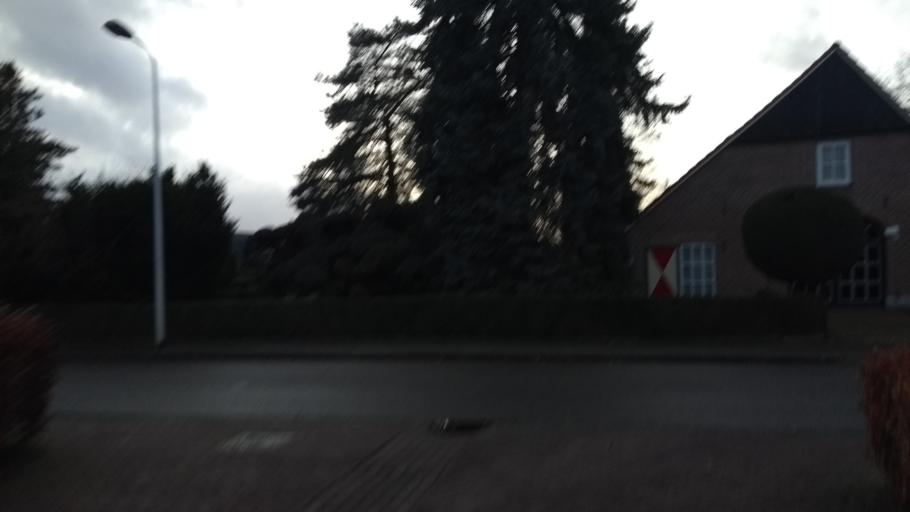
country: NL
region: Overijssel
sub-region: Gemeente Almelo
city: Almelo
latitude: 52.3746
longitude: 6.6903
